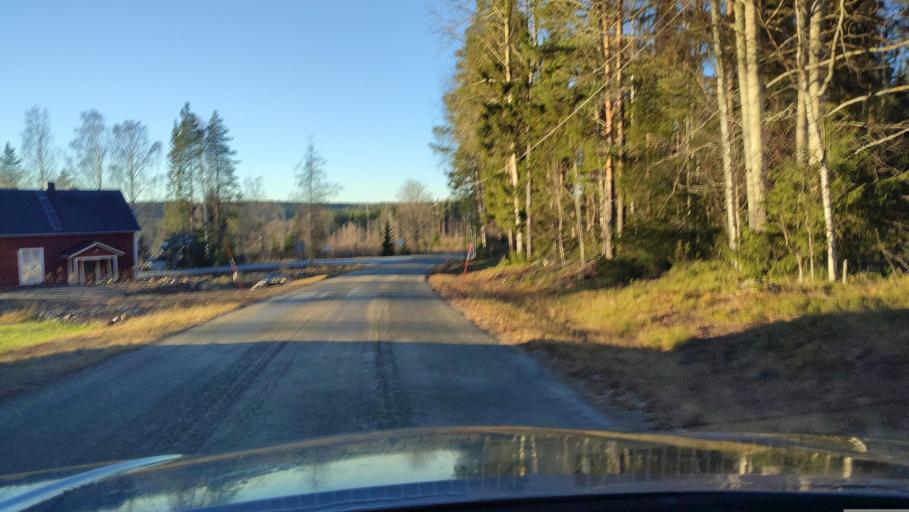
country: SE
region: Vaesterbotten
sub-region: Skelleftea Kommun
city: Viken
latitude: 64.7026
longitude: 20.9015
